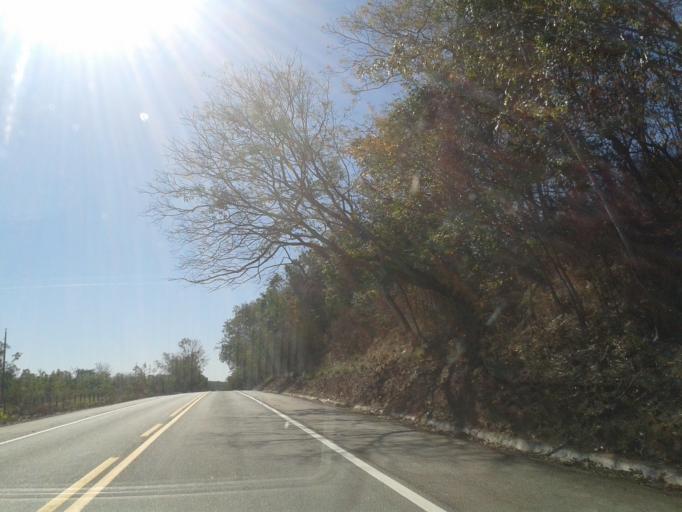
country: BR
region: Goias
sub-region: Goias
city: Goias
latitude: -15.8004
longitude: -50.1241
